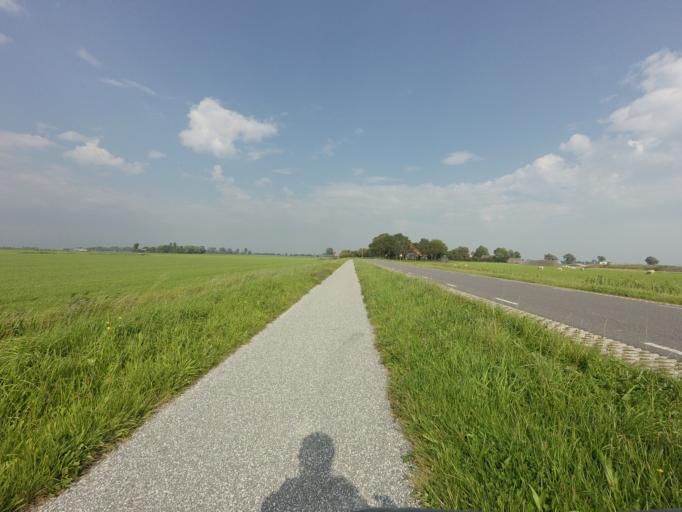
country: NL
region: Friesland
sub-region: Sudwest Fryslan
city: Bolsward
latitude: 53.0419
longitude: 5.5509
